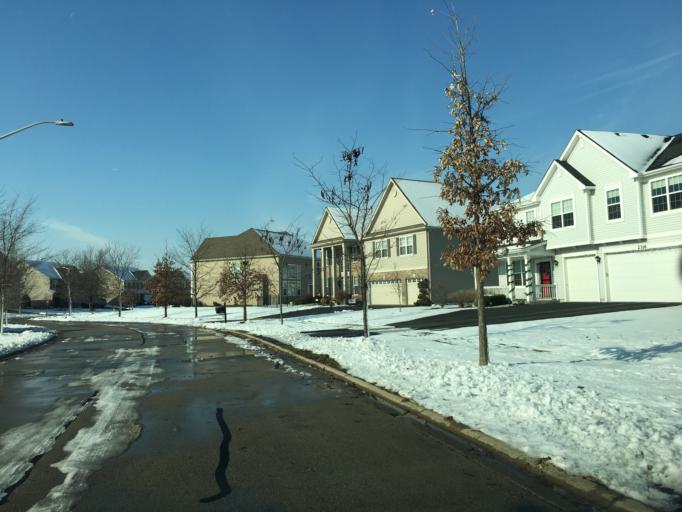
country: US
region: Illinois
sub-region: Will County
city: Plainfield
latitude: 41.6551
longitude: -88.1742
